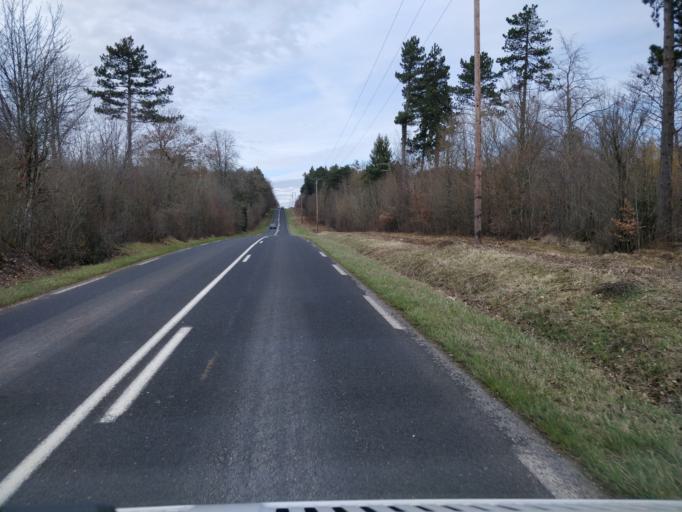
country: FR
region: Lorraine
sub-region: Departement de Meurthe-et-Moselle
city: Montauville
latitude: 48.9141
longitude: 5.9228
